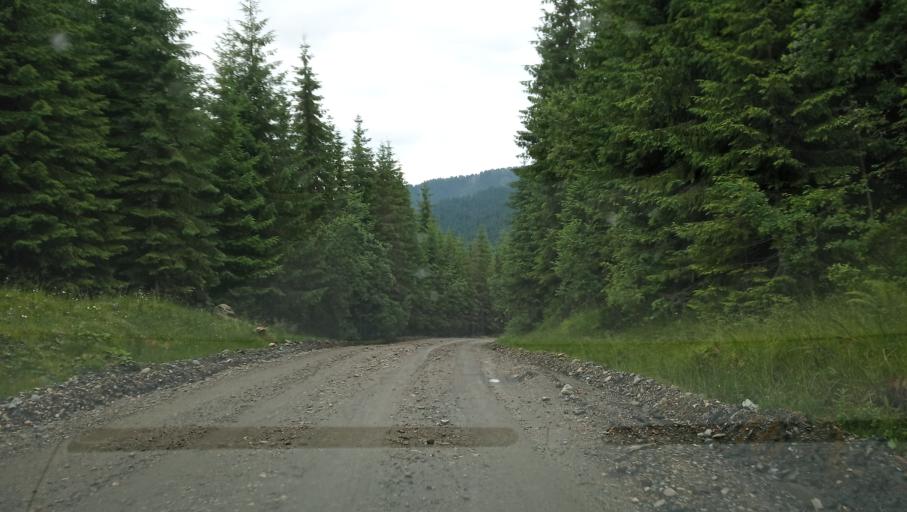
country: RO
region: Hunedoara
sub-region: Oras Petrila
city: Petrila
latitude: 45.4032
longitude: 23.5681
